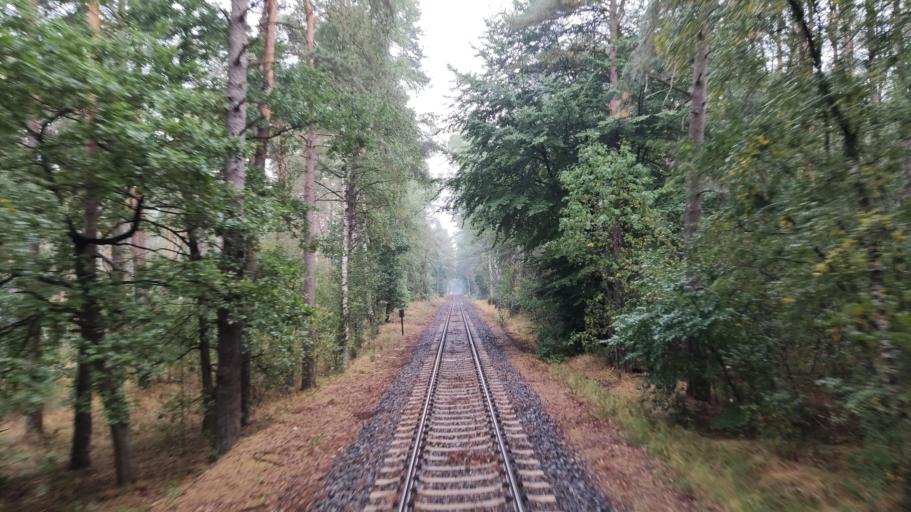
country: DE
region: Lower Saxony
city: Soltau
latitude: 53.0034
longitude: 9.8886
